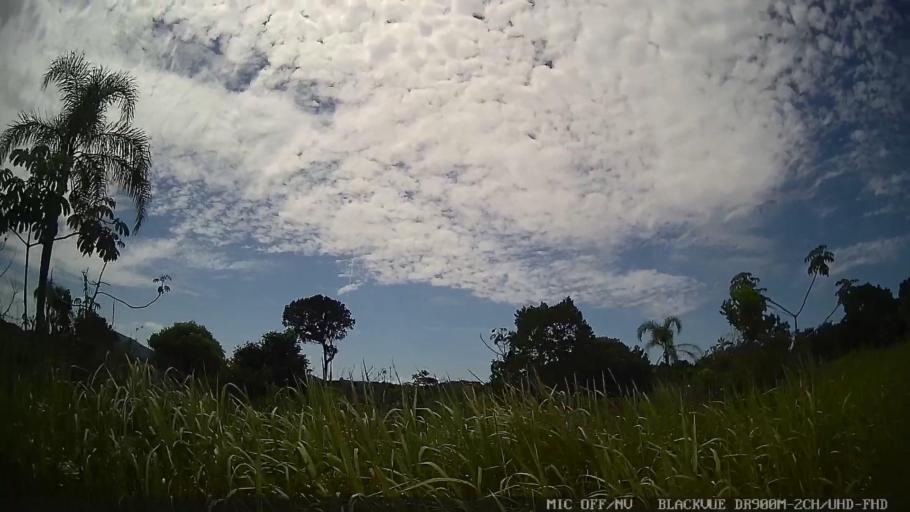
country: BR
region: Sao Paulo
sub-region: Iguape
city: Iguape
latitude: -24.7237
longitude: -47.5301
